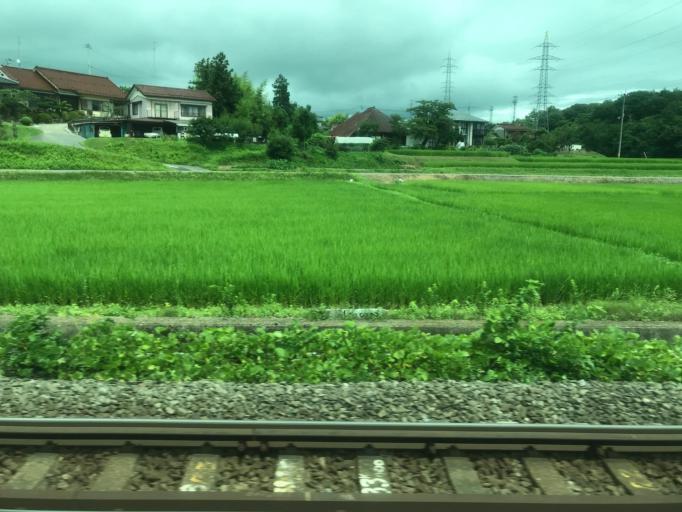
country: JP
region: Fukushima
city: Koriyama
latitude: 37.4510
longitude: 140.3841
